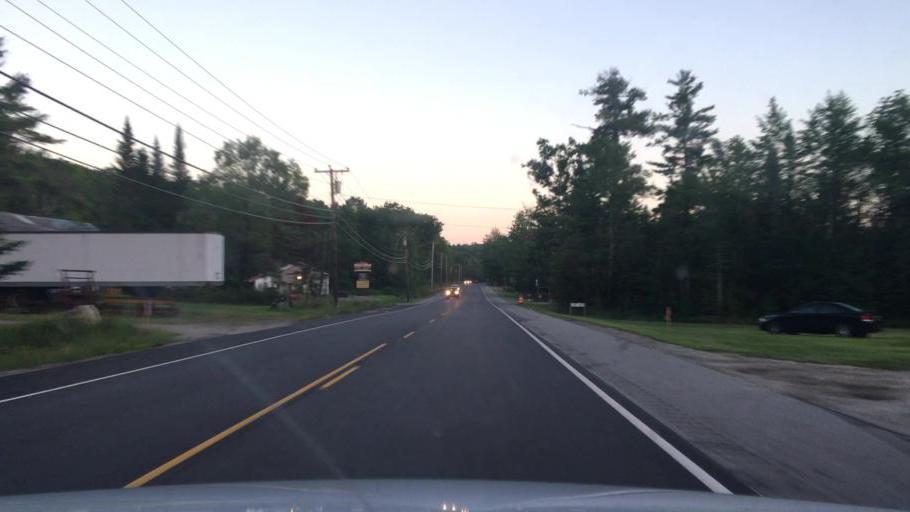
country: US
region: Maine
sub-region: Androscoggin County
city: Turner
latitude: 44.2224
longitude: -70.2487
